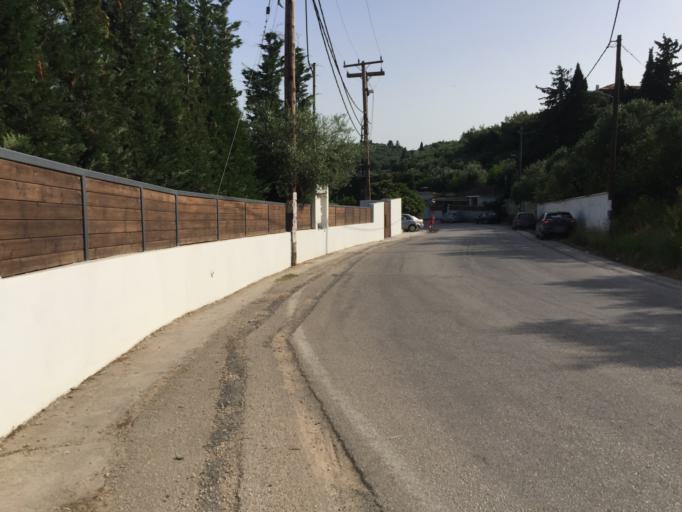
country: GR
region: Ionian Islands
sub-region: Nomos Zakynthou
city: Vanaton
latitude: 37.8208
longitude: 20.8575
